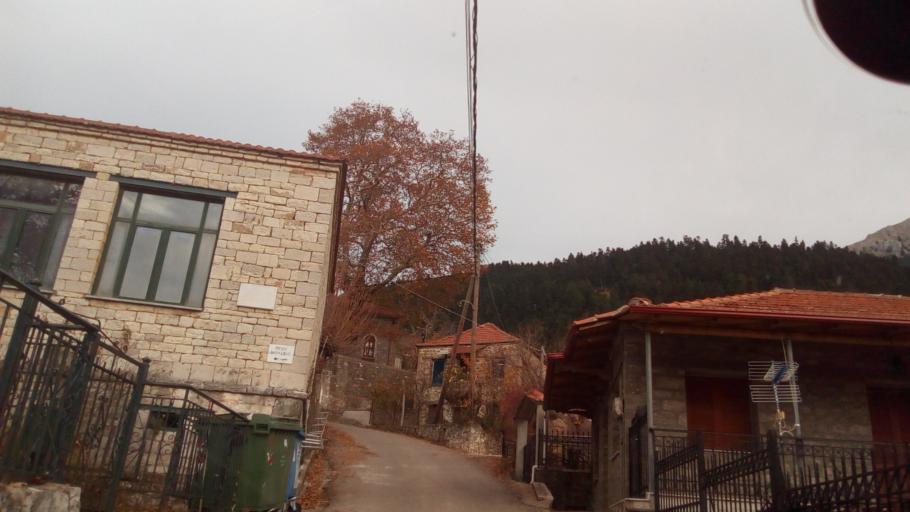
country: GR
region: West Greece
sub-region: Nomos Aitolias kai Akarnanias
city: Thermo
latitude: 38.6856
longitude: 21.8659
